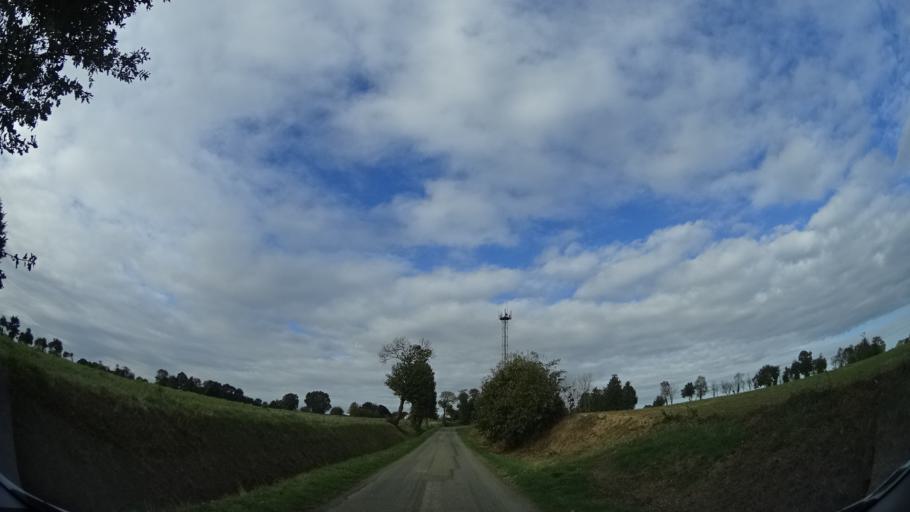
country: FR
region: Brittany
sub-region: Departement d'Ille-et-Vilaine
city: Vignoc
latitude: 48.2407
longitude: -1.8000
